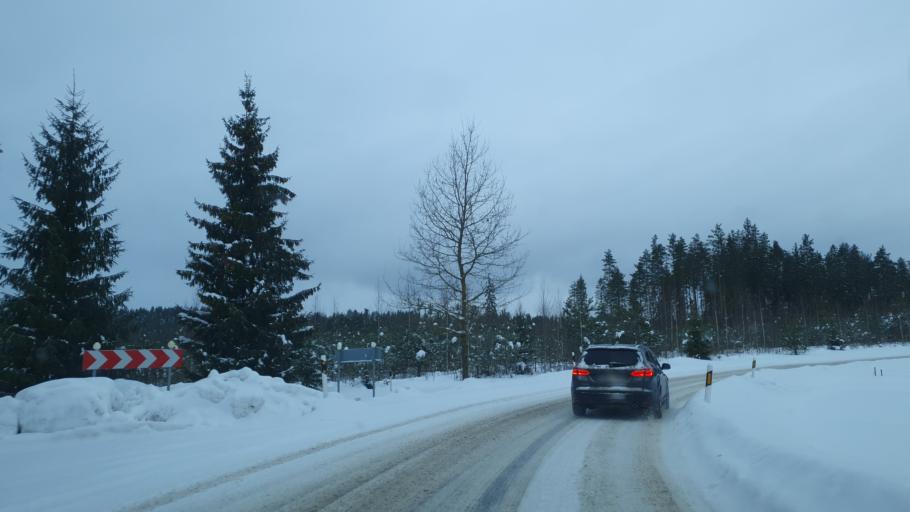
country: EE
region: Polvamaa
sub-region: Polva linn
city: Polva
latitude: 58.1063
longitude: 27.0870
